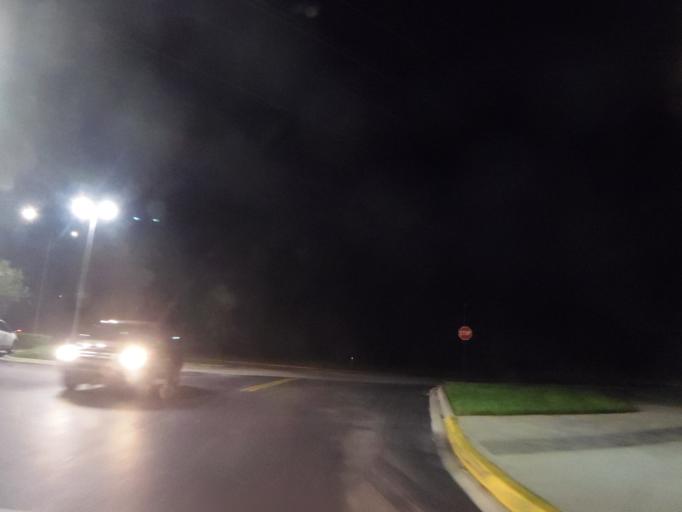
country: US
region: Florida
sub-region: Duval County
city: Jacksonville Beach
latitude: 30.2646
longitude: -81.5267
